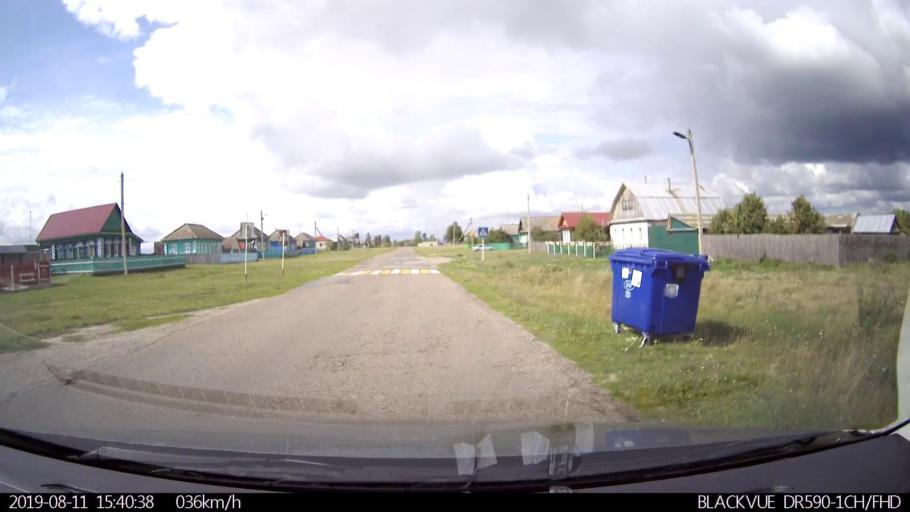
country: RU
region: Ulyanovsk
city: Ignatovka
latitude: 53.8702
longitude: 47.6499
